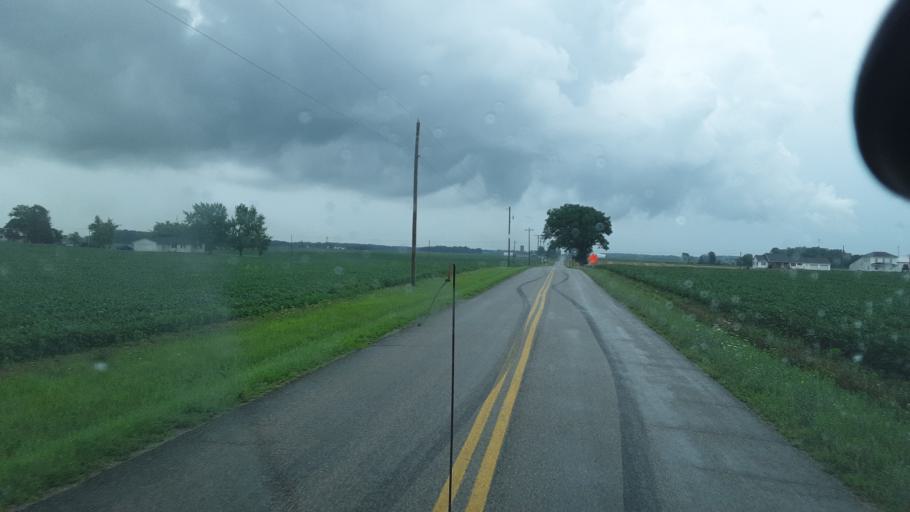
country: US
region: Ohio
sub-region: Williams County
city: Edgerton
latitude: 41.5590
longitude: -84.7884
